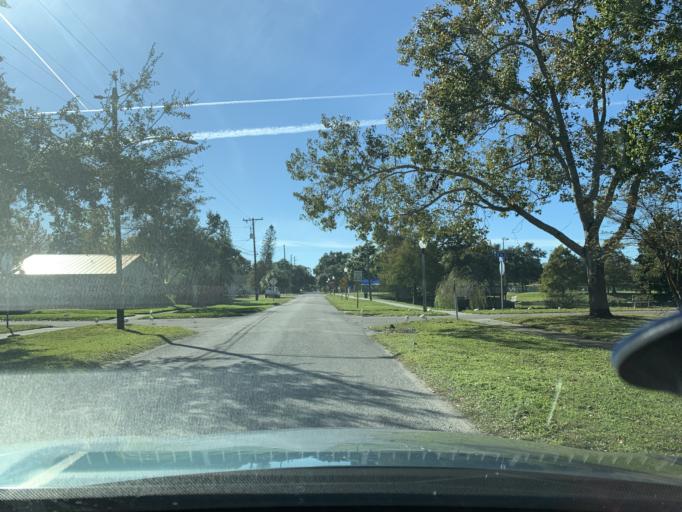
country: US
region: Florida
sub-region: Pinellas County
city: Gulfport
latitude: 27.7532
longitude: -82.7066
